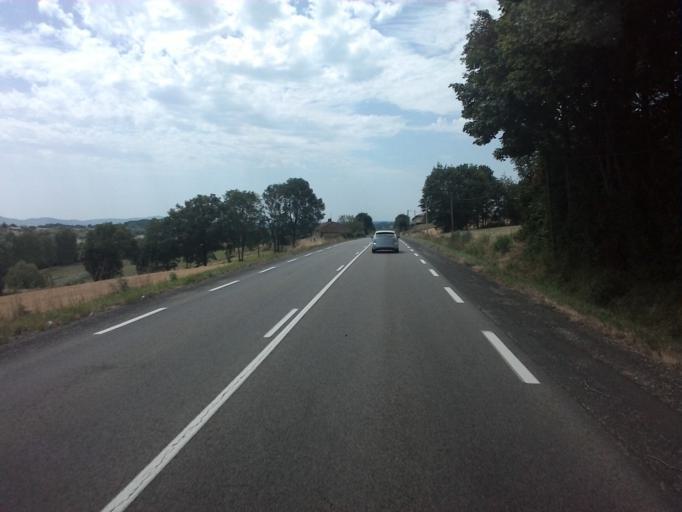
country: FR
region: Rhone-Alpes
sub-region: Departement de l'Ain
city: Coligny
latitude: 46.3733
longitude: 5.3407
